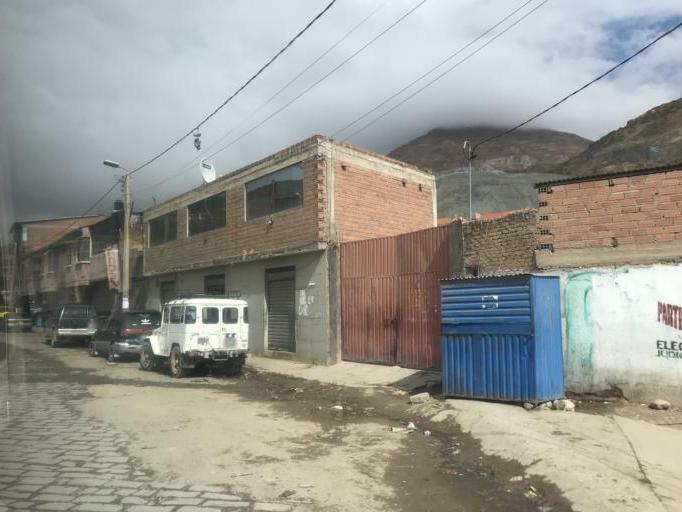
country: BO
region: Potosi
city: Potosi
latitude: -19.6006
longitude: -65.7475
